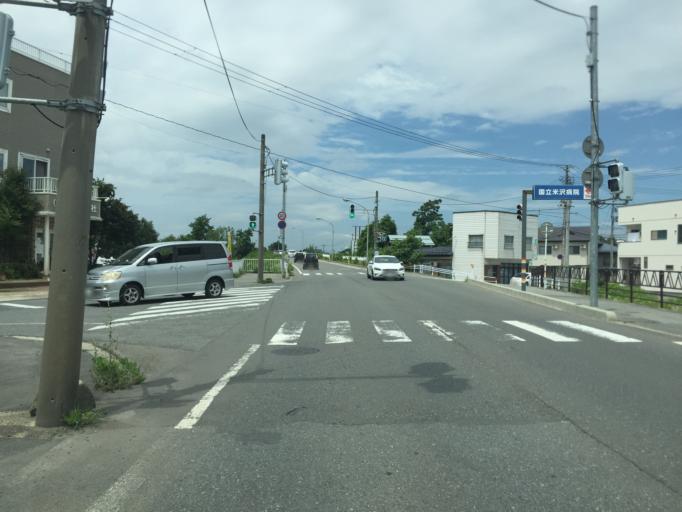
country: JP
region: Yamagata
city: Yonezawa
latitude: 37.9038
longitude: 140.1321
